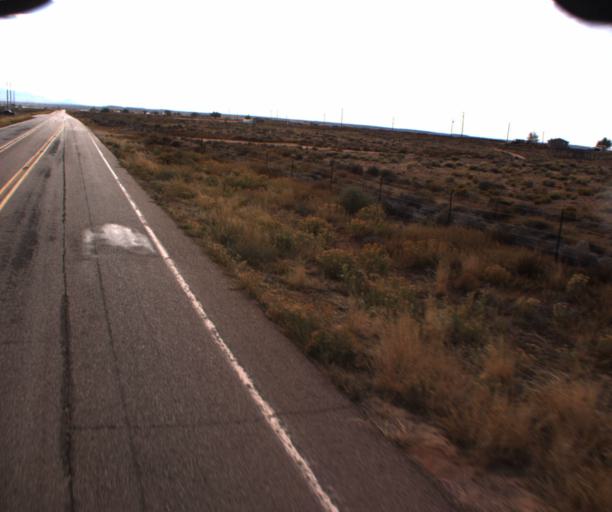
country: US
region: Arizona
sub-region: Apache County
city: Many Farms
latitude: 36.5160
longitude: -109.4837
